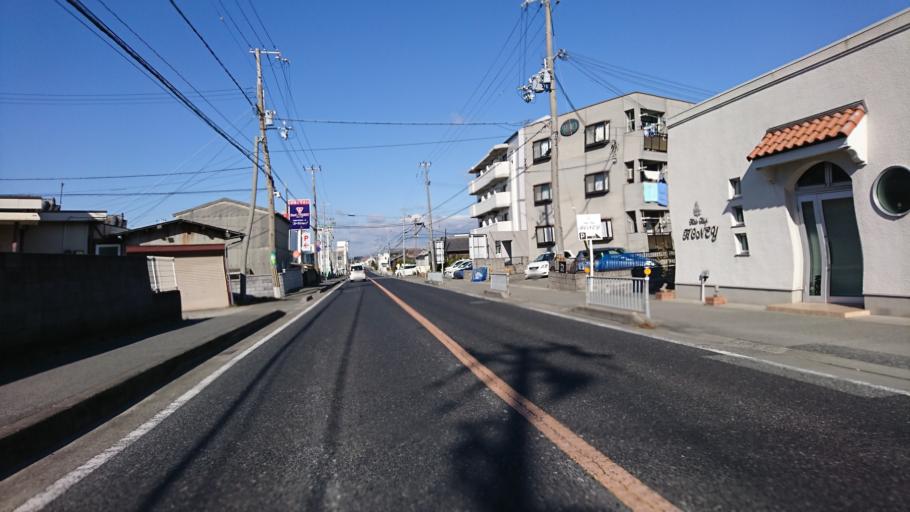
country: JP
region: Hyogo
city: Kakogawacho-honmachi
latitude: 34.7246
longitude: 134.8884
